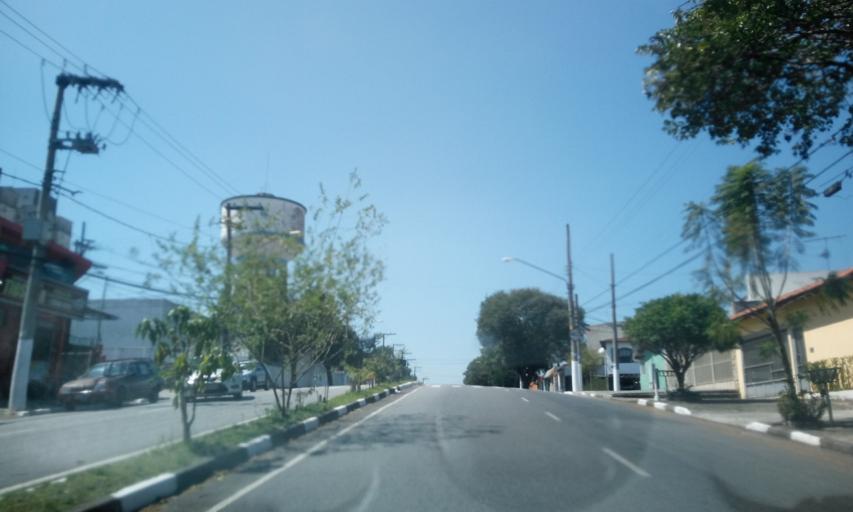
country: BR
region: Sao Paulo
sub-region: Sao Bernardo Do Campo
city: Sao Bernardo do Campo
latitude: -23.6993
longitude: -46.5693
